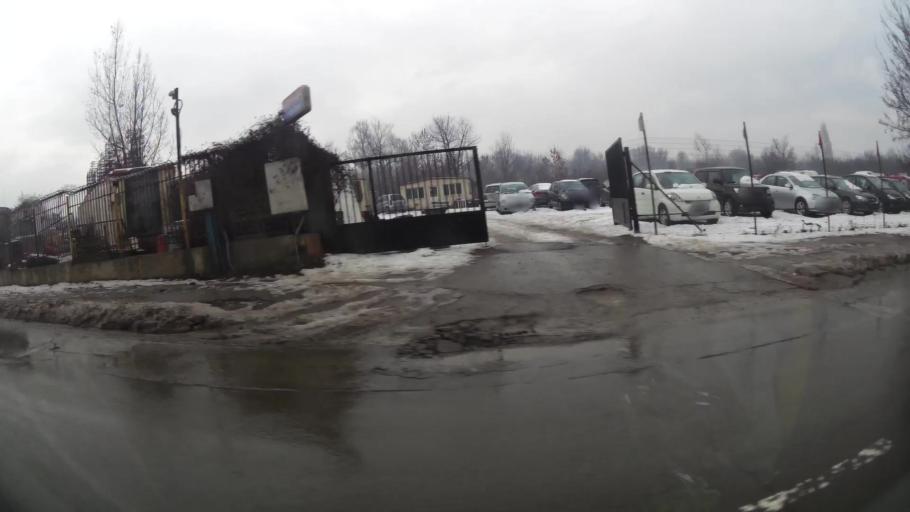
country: BG
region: Sofiya
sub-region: Obshtina Bozhurishte
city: Bozhurishte
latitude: 42.6877
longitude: 23.2404
